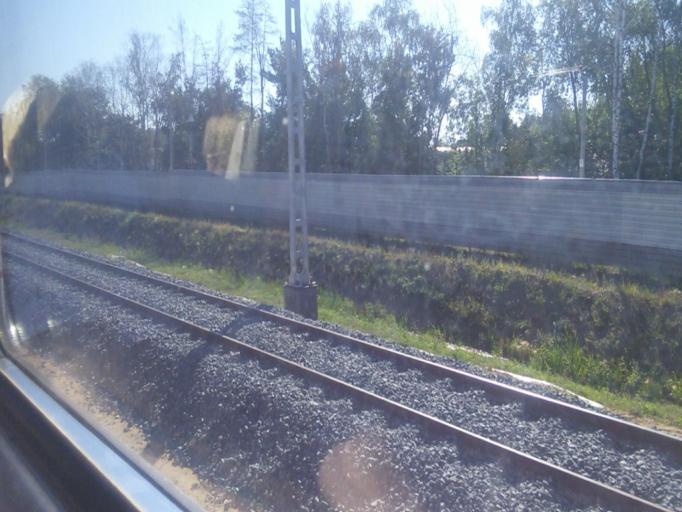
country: RU
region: Moskovskaya
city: Reutov
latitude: 55.7584
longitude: 37.8904
